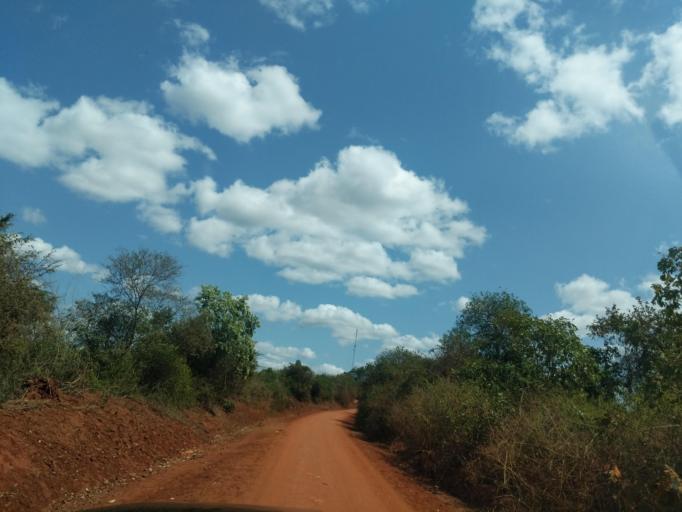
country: TZ
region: Tanga
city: Chanika
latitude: -5.5173
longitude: 38.3577
